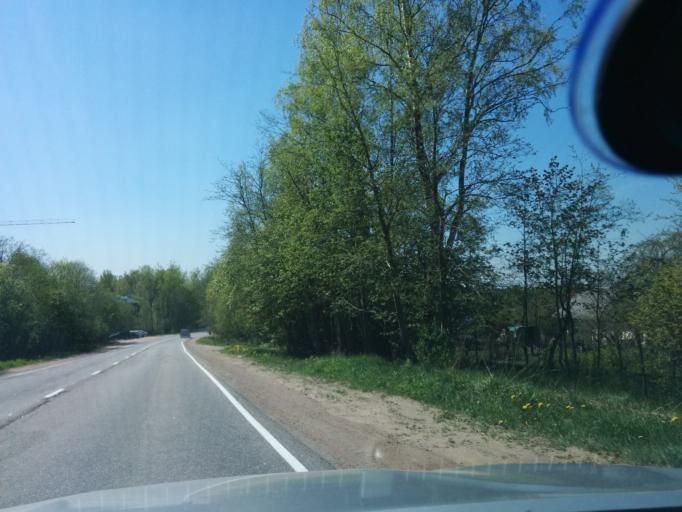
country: RU
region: Leningrad
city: Verkhniye Osel'ki
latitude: 60.2362
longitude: 30.4376
